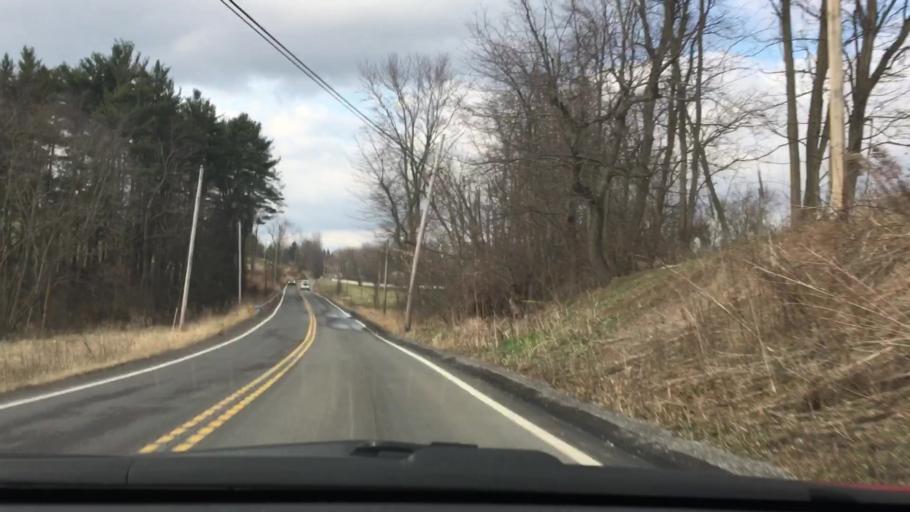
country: US
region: Pennsylvania
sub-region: Allegheny County
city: Enlow
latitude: 40.4306
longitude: -80.2045
